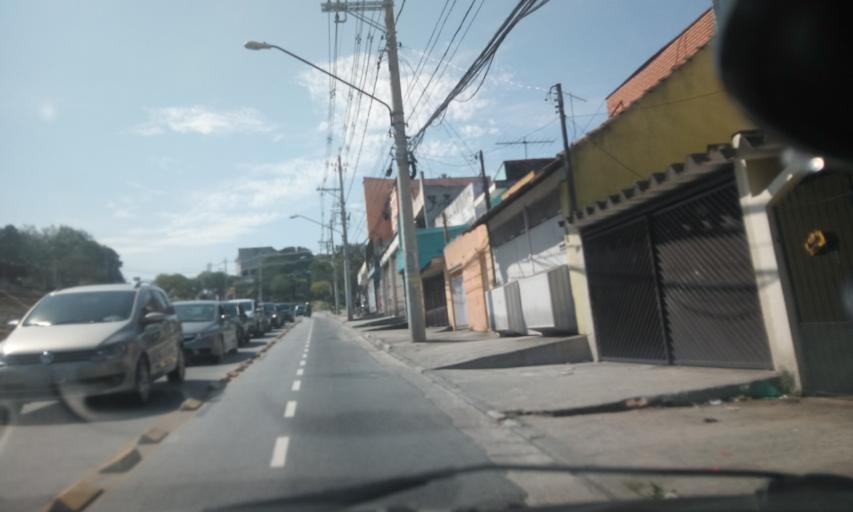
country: BR
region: Sao Paulo
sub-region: Sao Bernardo Do Campo
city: Sao Bernardo do Campo
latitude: -23.7202
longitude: -46.5371
